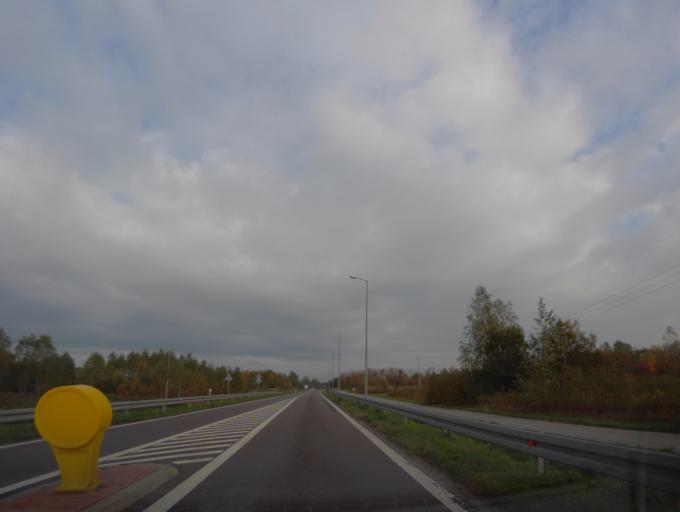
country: PL
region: Lublin Voivodeship
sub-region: Powiat bilgorajski
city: Frampol
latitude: 50.6562
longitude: 22.6814
